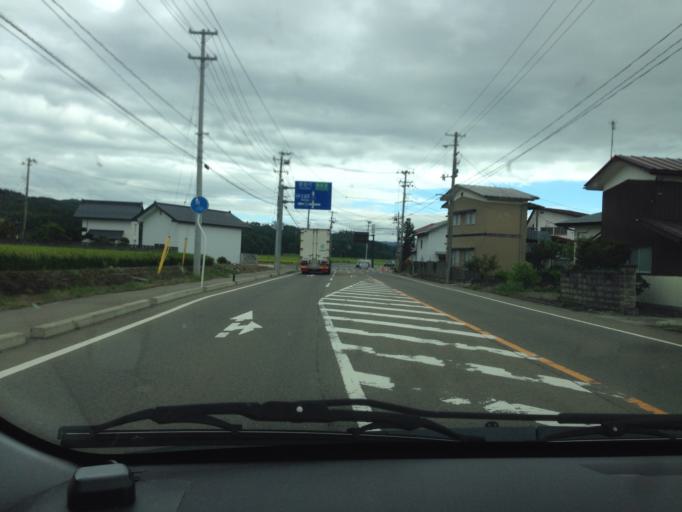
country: JP
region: Fukushima
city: Kitakata
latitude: 37.5899
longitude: 139.9078
